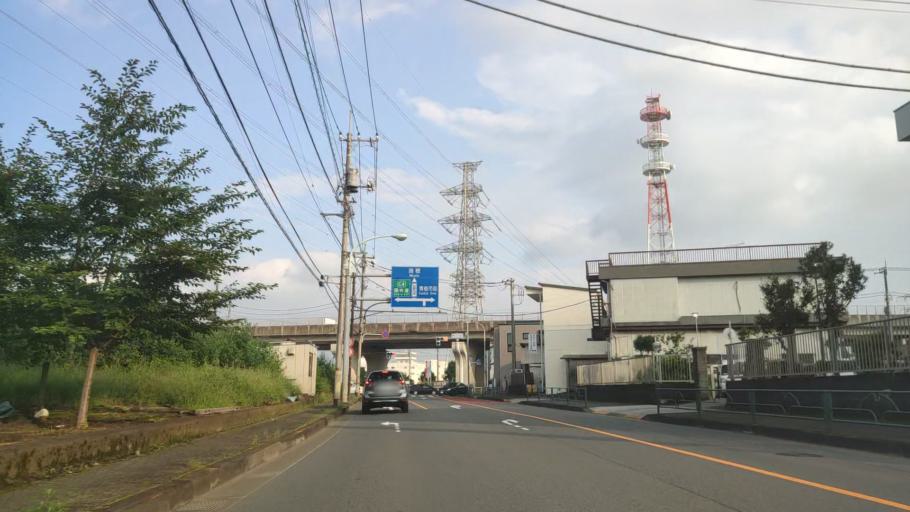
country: JP
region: Saitama
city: Hanno
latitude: 35.7965
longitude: 139.3170
